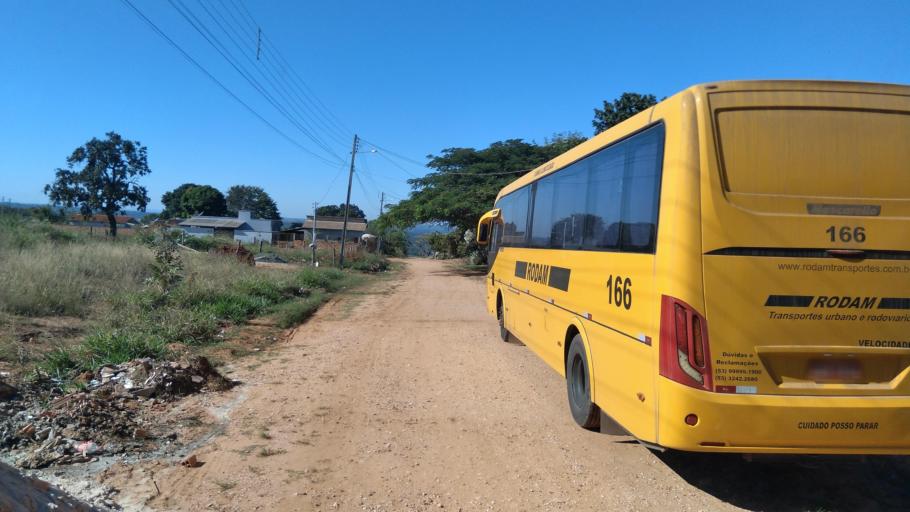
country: BR
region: Goias
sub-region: Mineiros
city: Mineiros
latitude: -17.5928
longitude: -52.5562
